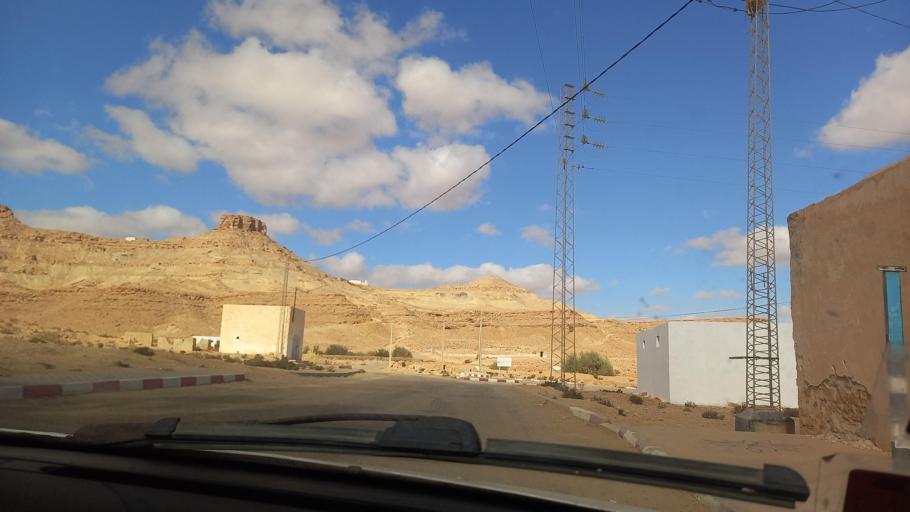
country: TN
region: Tataouine
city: Tataouine
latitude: 32.9837
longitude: 10.2611
